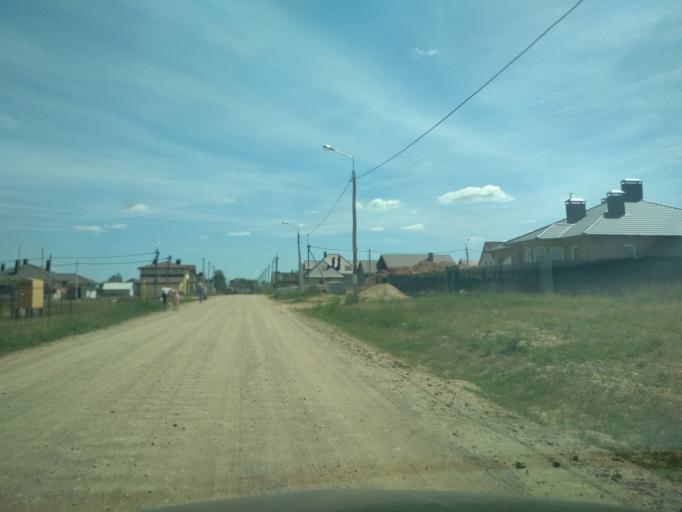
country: BY
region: Minsk
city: Mar''ina Horka
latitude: 53.5116
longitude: 28.1572
